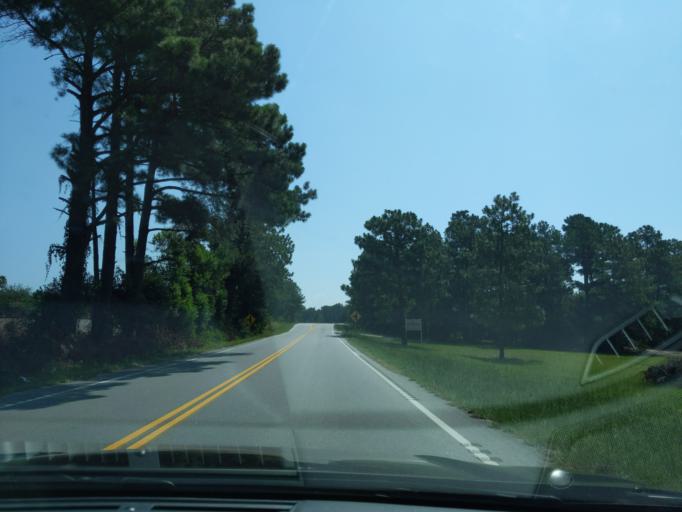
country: US
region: South Carolina
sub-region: Lexington County
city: Red Bank
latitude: 33.9316
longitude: -81.3108
